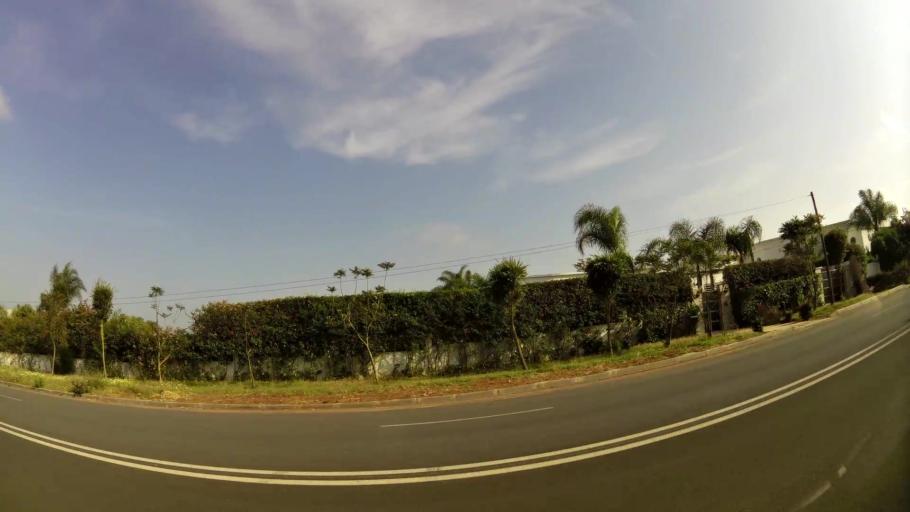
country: MA
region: Rabat-Sale-Zemmour-Zaer
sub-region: Rabat
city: Rabat
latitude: 33.9336
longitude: -6.8072
